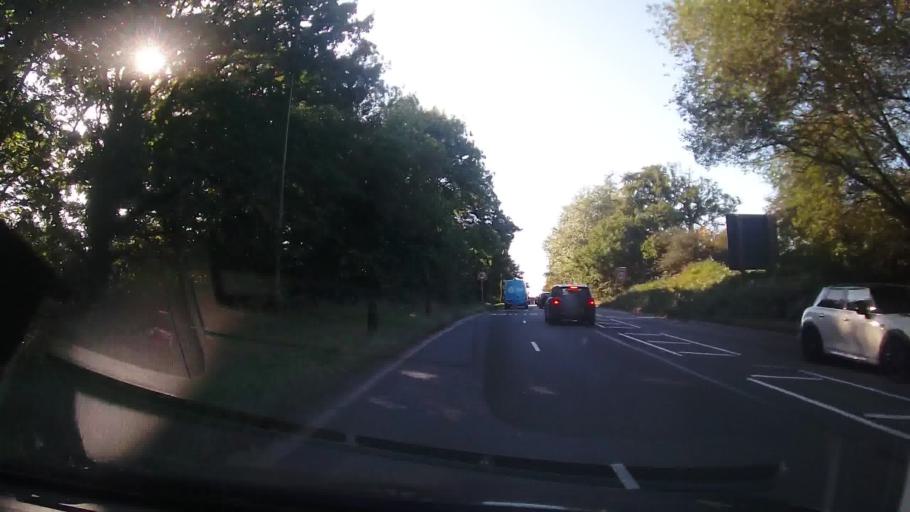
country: GB
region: England
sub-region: Buckinghamshire
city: Beaconsfield
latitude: 51.6017
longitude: -0.6271
